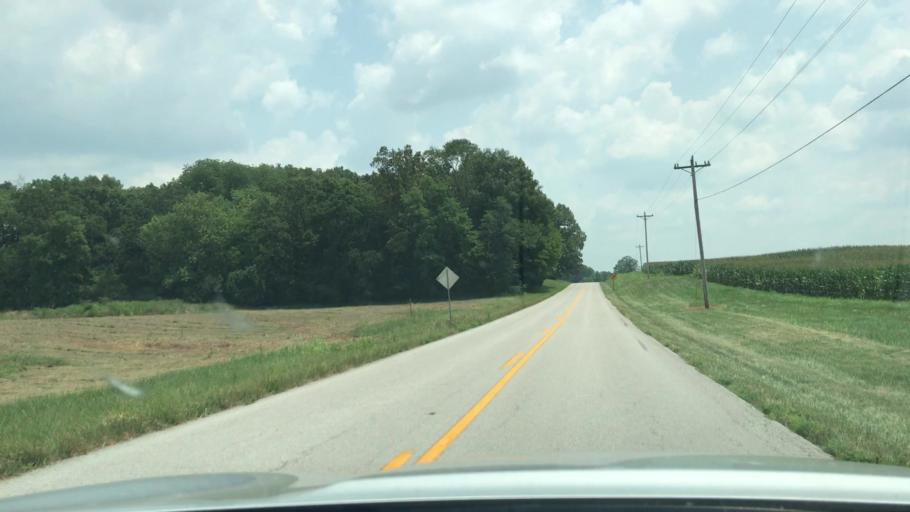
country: US
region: Kentucky
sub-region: Todd County
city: Elkton
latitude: 36.7604
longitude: -87.1013
